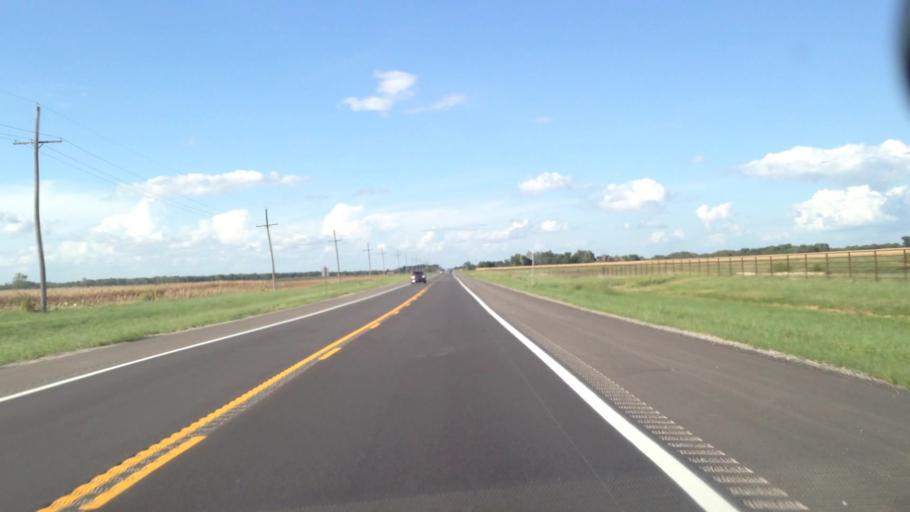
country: US
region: Kansas
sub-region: Franklin County
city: Ottawa
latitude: 38.5110
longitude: -95.2683
